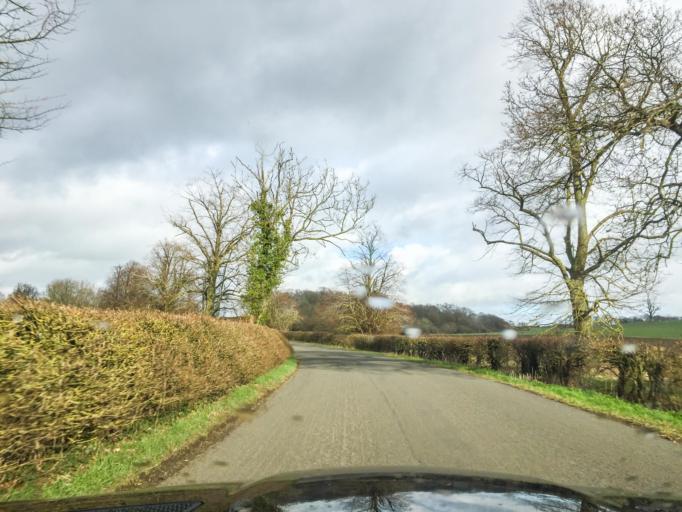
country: GB
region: England
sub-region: Warwickshire
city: Shipston on Stour
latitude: 52.0908
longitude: -1.5930
